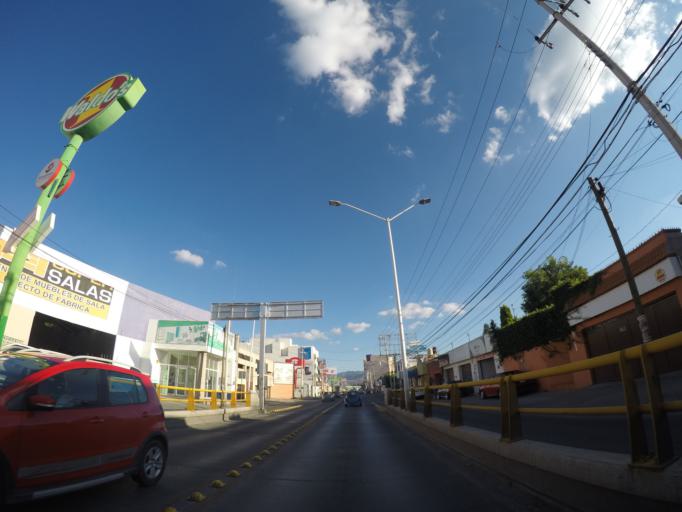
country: MX
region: San Luis Potosi
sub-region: San Luis Potosi
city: San Luis Potosi
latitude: 22.1640
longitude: -101.0009
